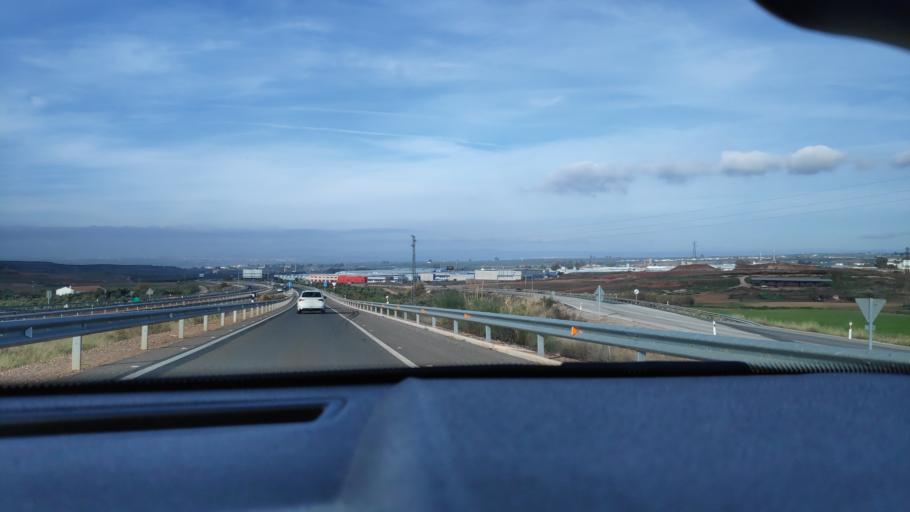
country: ES
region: Andalusia
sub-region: Provincia de Jaen
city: Linares
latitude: 38.0822
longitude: -3.6466
